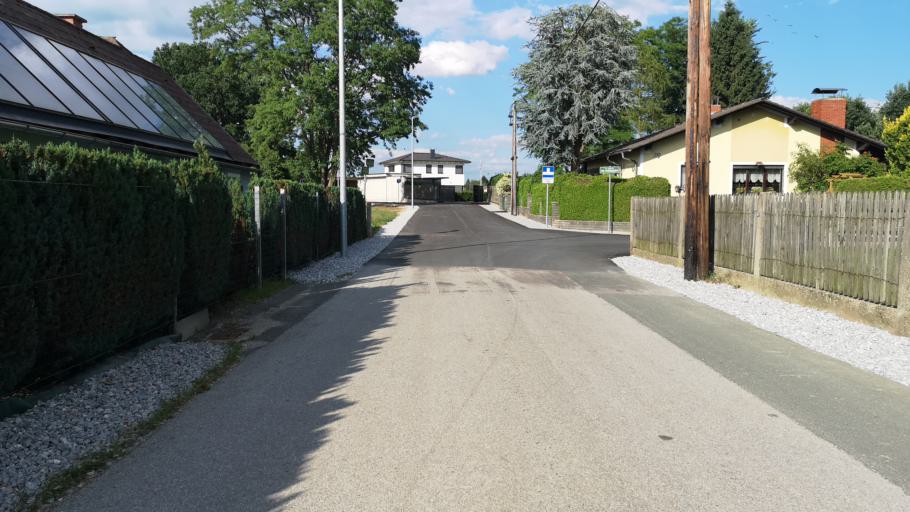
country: AT
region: Styria
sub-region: Politischer Bezirk Graz-Umgebung
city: Feldkirchen bei Graz
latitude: 47.0250
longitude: 15.4598
